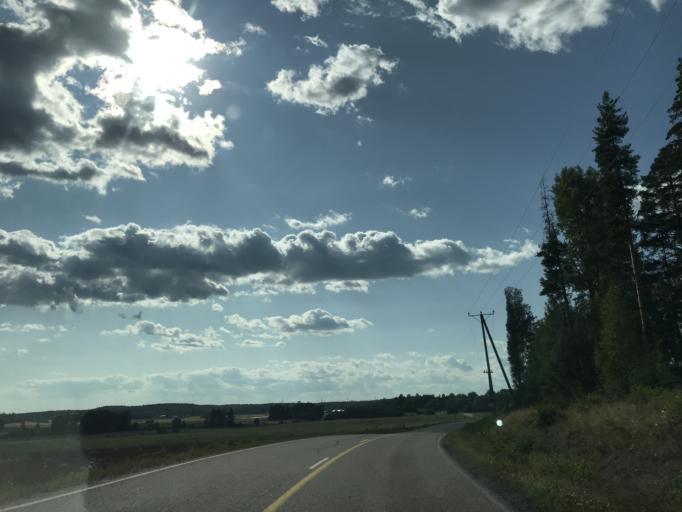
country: FI
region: Uusimaa
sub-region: Helsinki
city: Nurmijaervi
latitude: 60.4517
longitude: 24.6311
